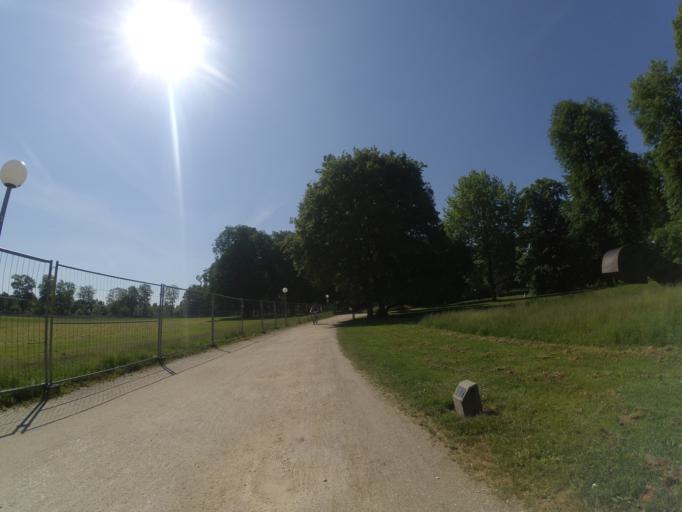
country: DE
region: Bavaria
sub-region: Swabia
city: Neu-Ulm
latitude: 48.4099
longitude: 10.0141
